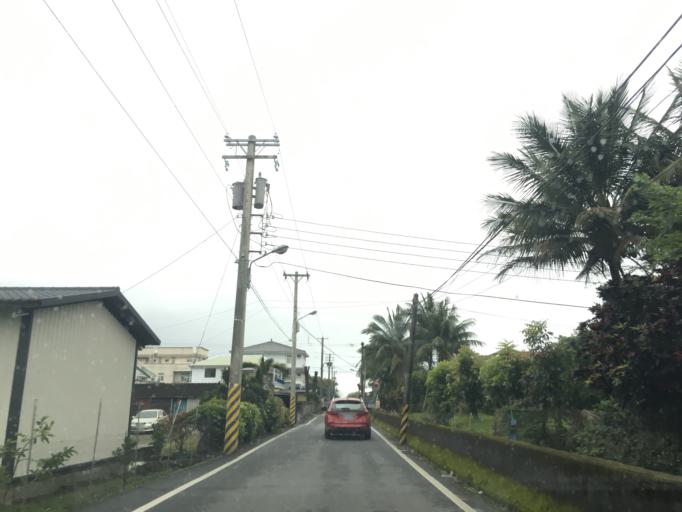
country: TW
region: Taiwan
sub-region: Hualien
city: Hualian
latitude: 23.9852
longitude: 121.5677
